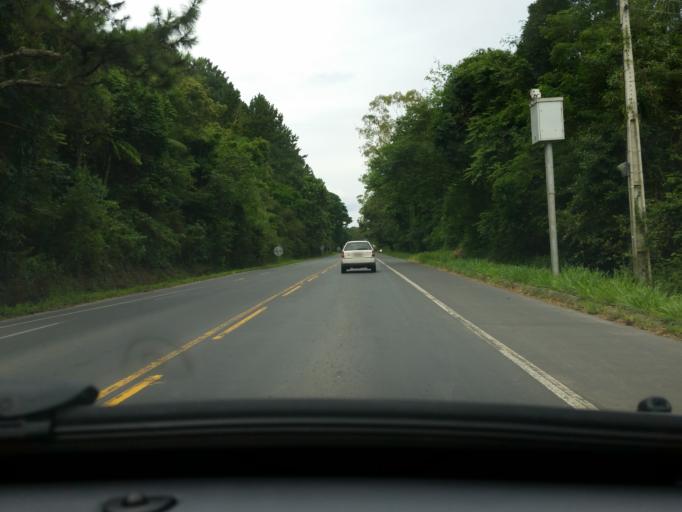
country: BR
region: Santa Catarina
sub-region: Rio Do Sul
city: Rio do Sul
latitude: -27.2566
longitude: -49.7110
